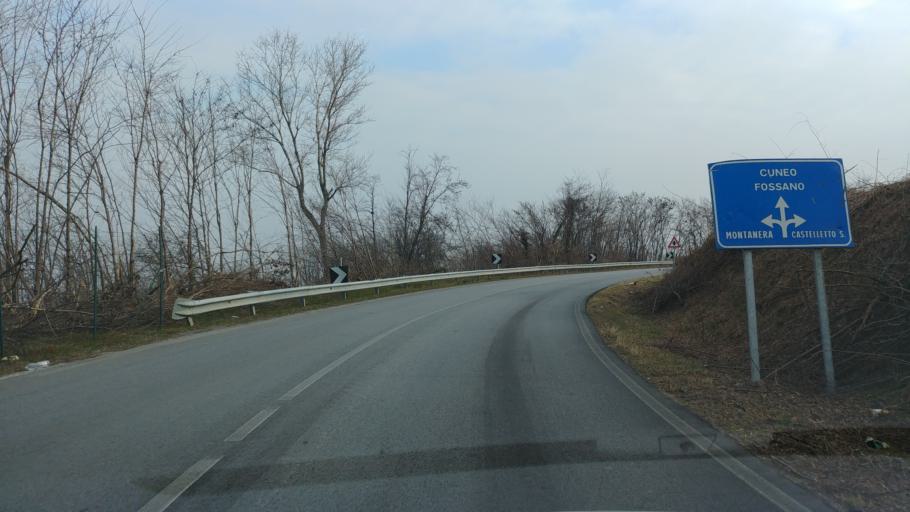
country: IT
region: Piedmont
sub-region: Provincia di Cuneo
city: Castelletto Stura
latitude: 44.4499
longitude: 7.6451
